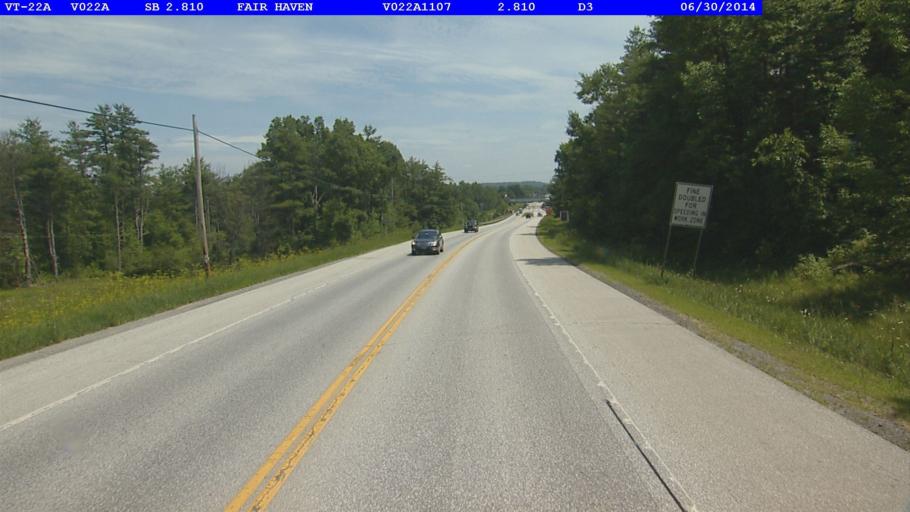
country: US
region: Vermont
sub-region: Rutland County
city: Fair Haven
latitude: 43.6094
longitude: -73.2819
